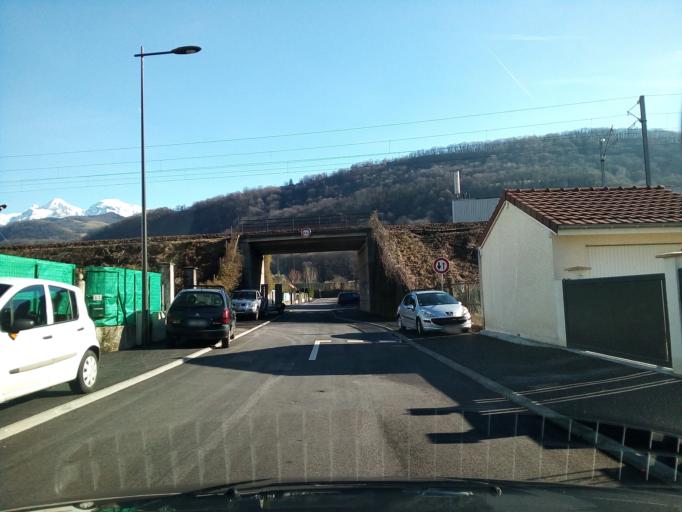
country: FR
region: Rhone-Alpes
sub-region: Departement de l'Isere
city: Saint-Martin-d'Heres
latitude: 45.1782
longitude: 5.7694
